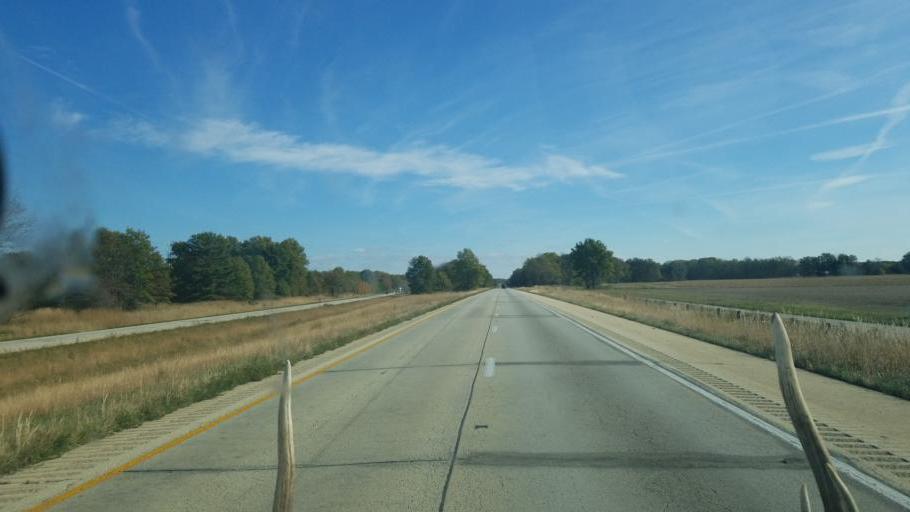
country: US
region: Illinois
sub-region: Effingham County
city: Altamont
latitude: 39.0751
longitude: -88.6457
